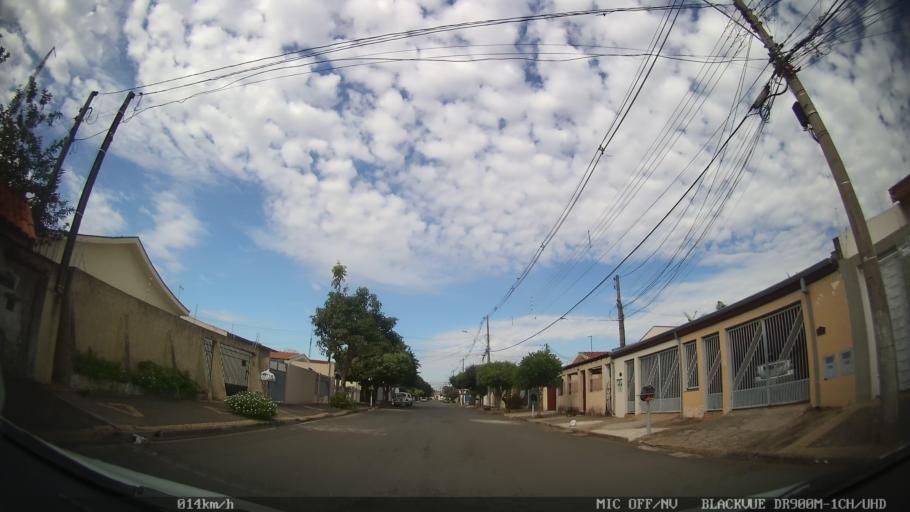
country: BR
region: Sao Paulo
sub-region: Americana
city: Americana
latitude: -22.7209
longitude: -47.3601
